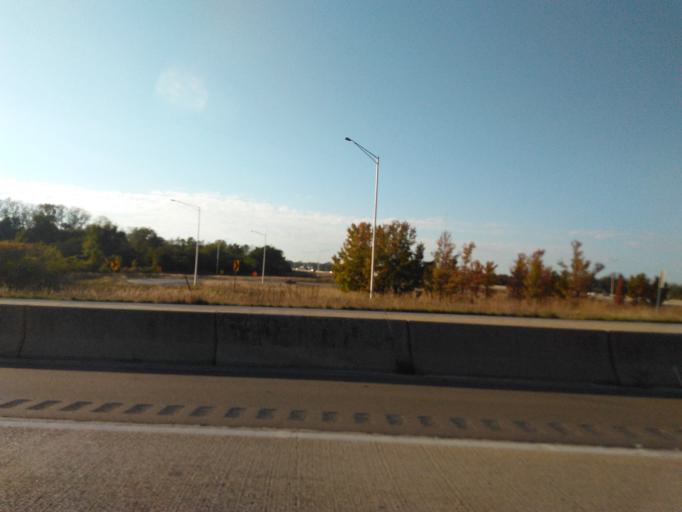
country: US
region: Illinois
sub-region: Saint Clair County
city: Washington Park
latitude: 38.6167
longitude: -90.0702
